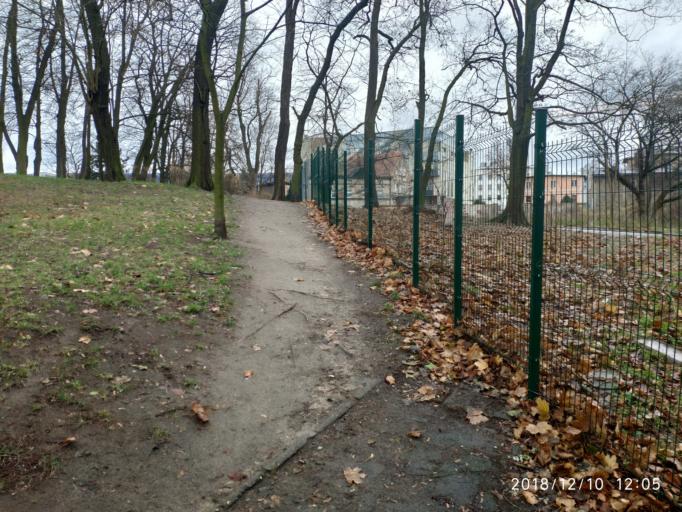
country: PL
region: Lubusz
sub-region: Zielona Gora
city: Zielona Gora
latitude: 51.9407
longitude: 15.5110
